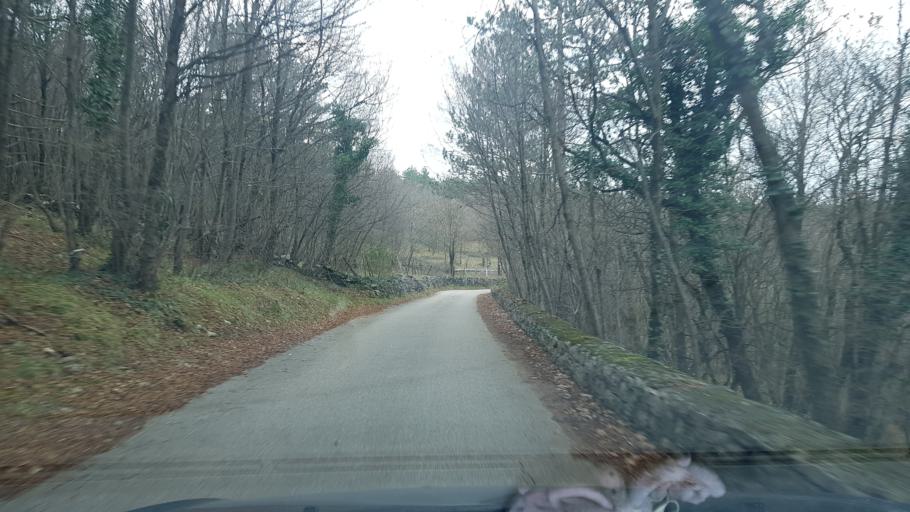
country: IT
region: Friuli Venezia Giulia
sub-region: Provincia di Trieste
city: Zolla
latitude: 45.7220
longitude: 13.8007
